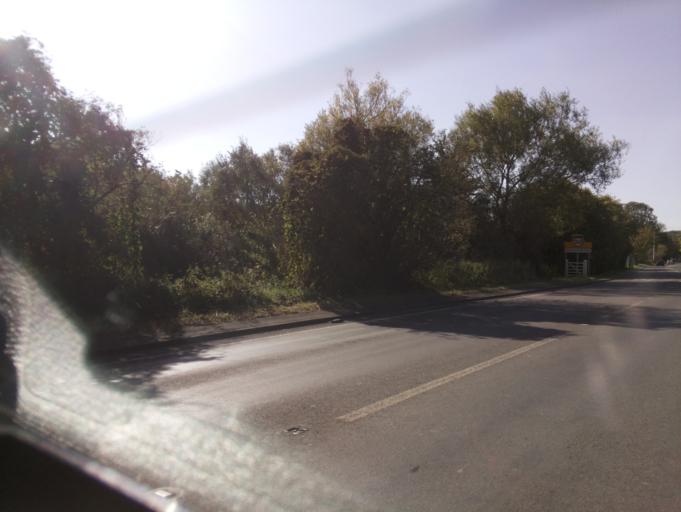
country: GB
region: England
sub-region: Hampshire
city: Tadley
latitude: 51.3968
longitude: -1.1709
